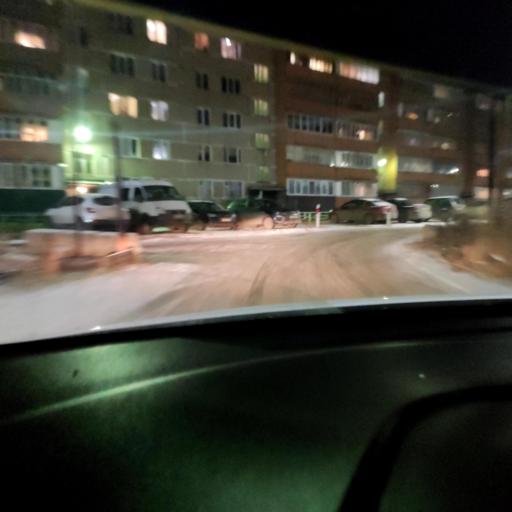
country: RU
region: Tatarstan
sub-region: Gorod Kazan'
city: Kazan
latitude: 55.7182
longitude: 49.0972
